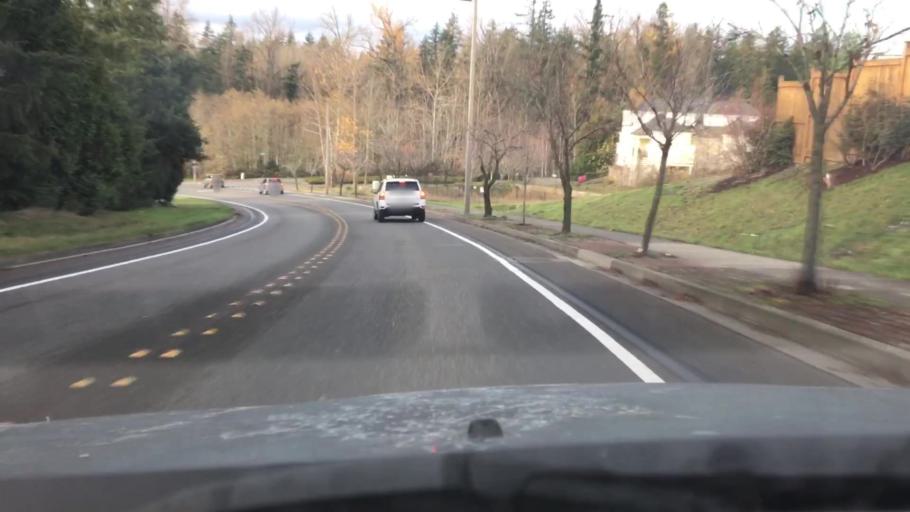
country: US
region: Washington
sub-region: Whatcom County
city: Geneva
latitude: 48.7744
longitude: -122.4306
